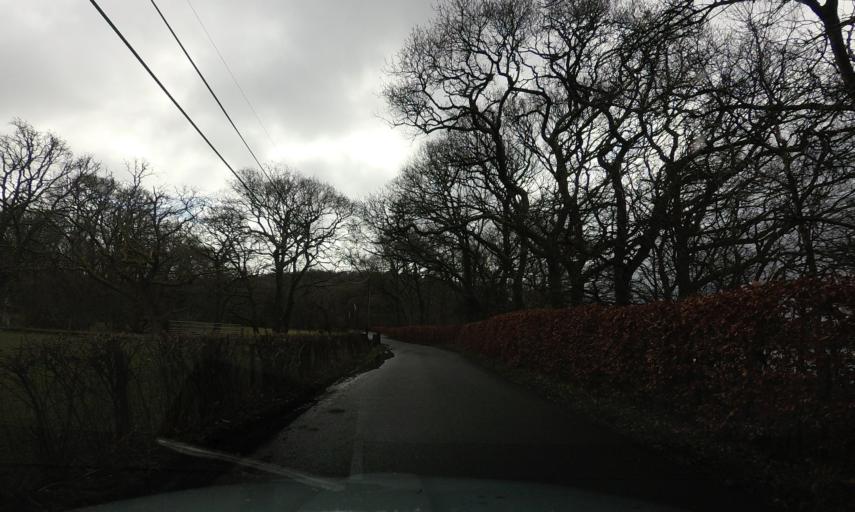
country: GB
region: Scotland
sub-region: West Dunbartonshire
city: Balloch
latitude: 56.0974
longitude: -4.5558
